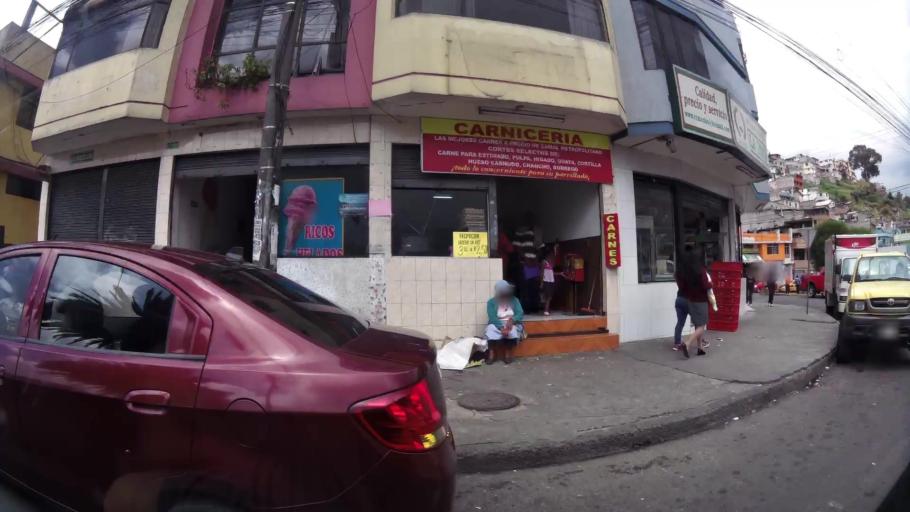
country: EC
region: Pichincha
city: Quito
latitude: -0.2475
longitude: -78.5071
